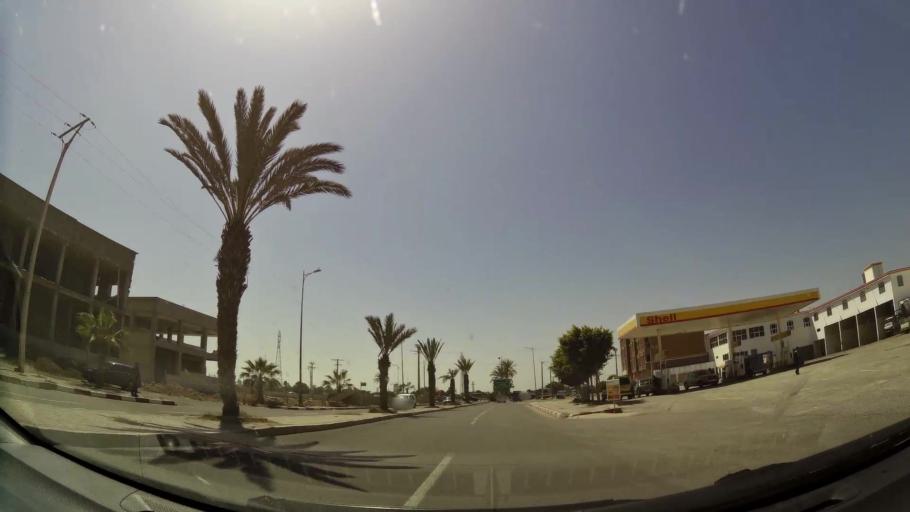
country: MA
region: Souss-Massa-Draa
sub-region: Inezgane-Ait Mellou
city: Inezgane
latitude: 30.3115
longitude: -9.5027
